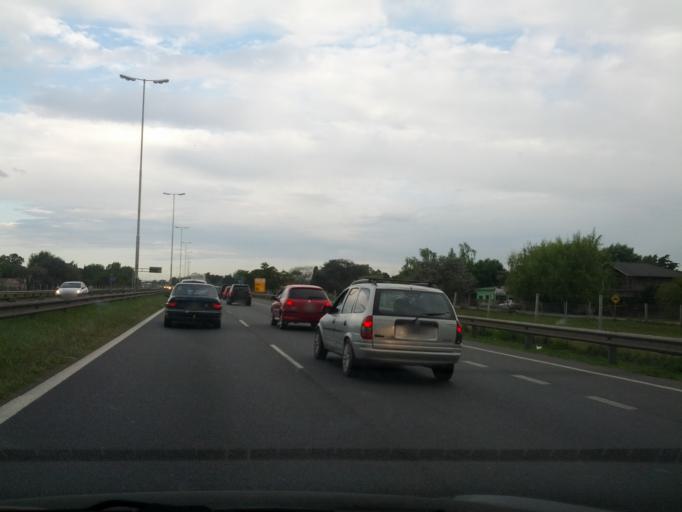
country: AR
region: Buenos Aires
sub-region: Partido de General Rodriguez
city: General Rodriguez
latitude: -34.5968
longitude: -58.9335
